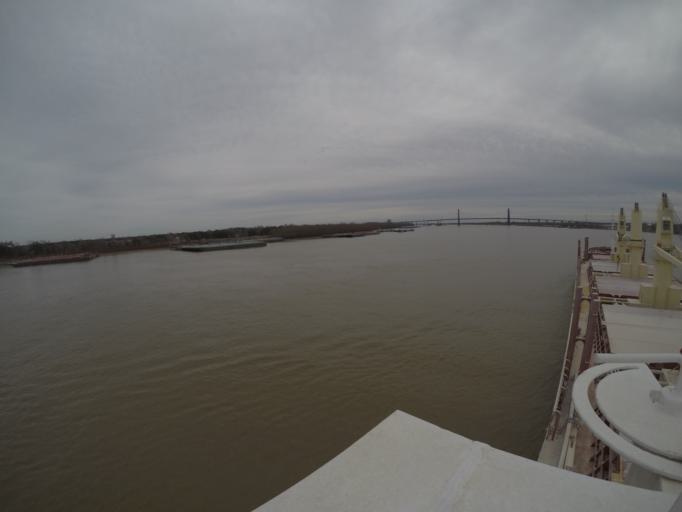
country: US
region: Louisiana
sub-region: Saint Charles Parish
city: New Sarpy
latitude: 29.9532
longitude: -90.3939
